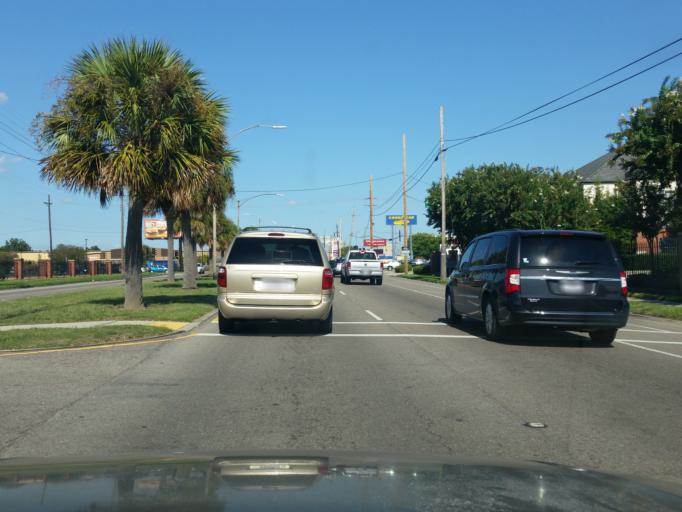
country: US
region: Louisiana
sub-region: Orleans Parish
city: New Orleans
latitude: 30.0033
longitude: -90.0413
